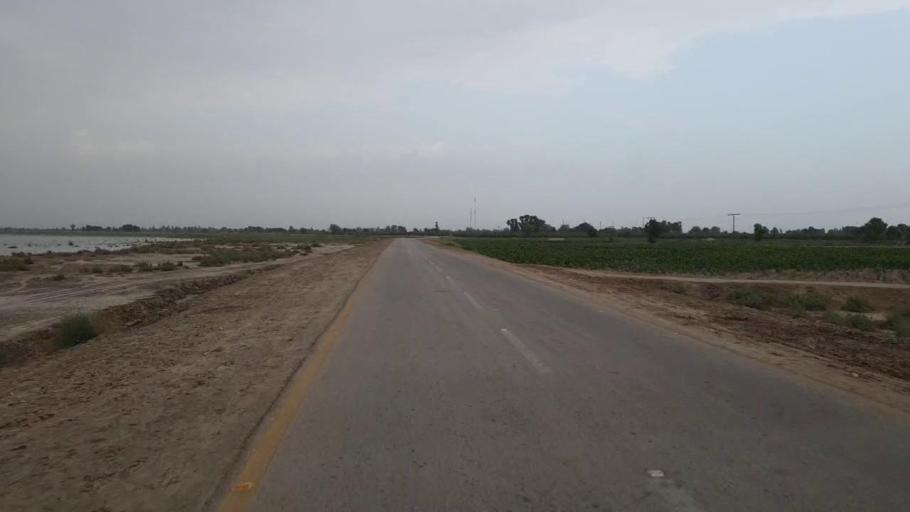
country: PK
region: Sindh
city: Bandhi
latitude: 26.5790
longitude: 68.2773
